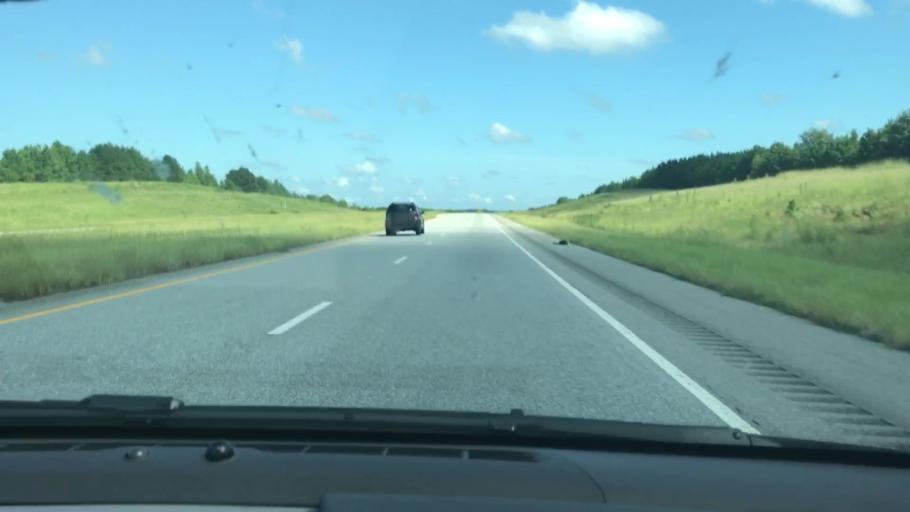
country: US
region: Alabama
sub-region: Barbour County
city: Eufaula
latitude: 32.1743
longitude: -85.1769
